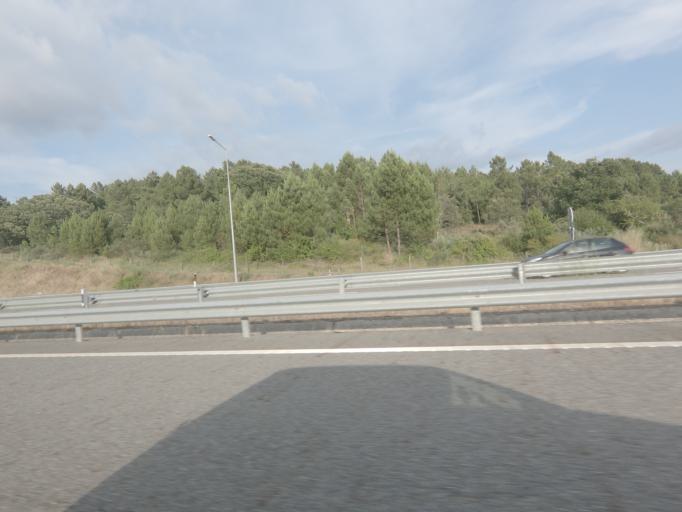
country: PT
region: Vila Real
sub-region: Boticas
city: Boticas
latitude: 41.6705
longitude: -7.5694
